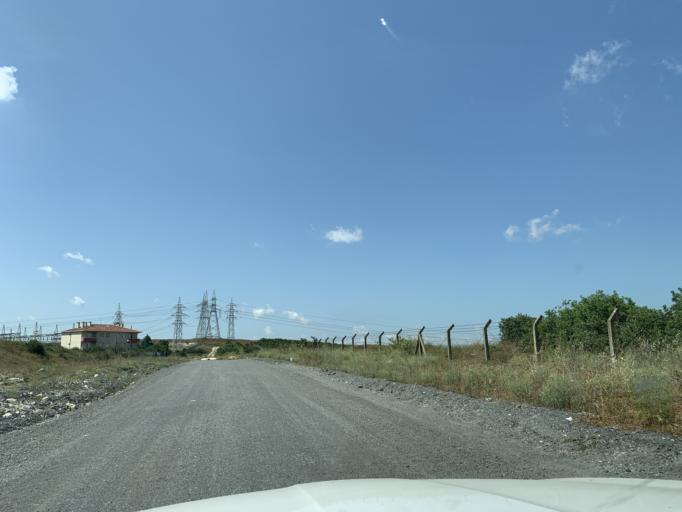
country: TR
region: Istanbul
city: Esenyurt
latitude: 41.0866
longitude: 28.6930
